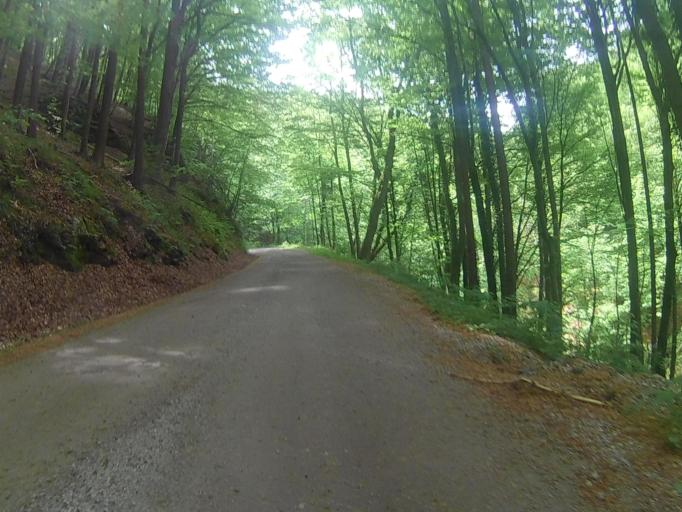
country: SI
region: Slovenska Bistrica
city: Zgornja Polskava
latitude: 46.4554
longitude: 15.5745
